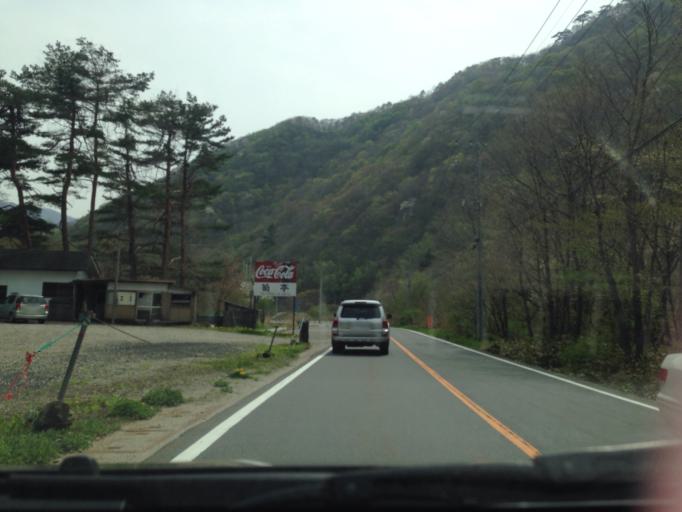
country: JP
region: Tochigi
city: Nikko
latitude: 37.0258
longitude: 139.7276
